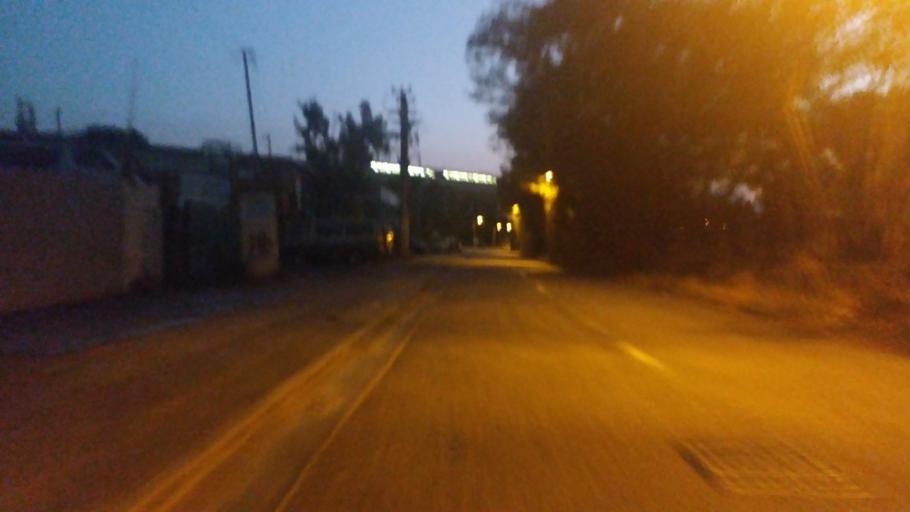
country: HK
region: Yuen Long
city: Yuen Long Kau Hui
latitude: 22.4443
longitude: 113.9969
